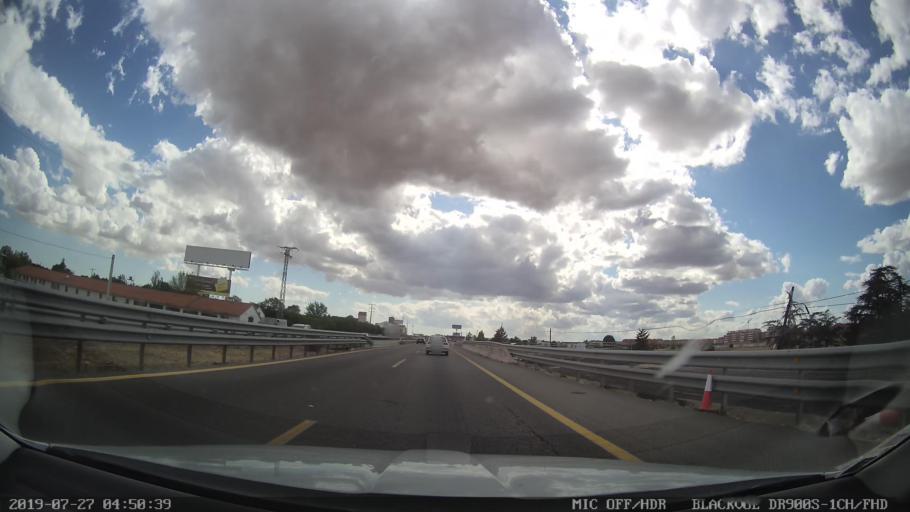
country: ES
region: Madrid
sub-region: Provincia de Madrid
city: Navalcarnero
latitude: 40.2960
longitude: -3.9701
